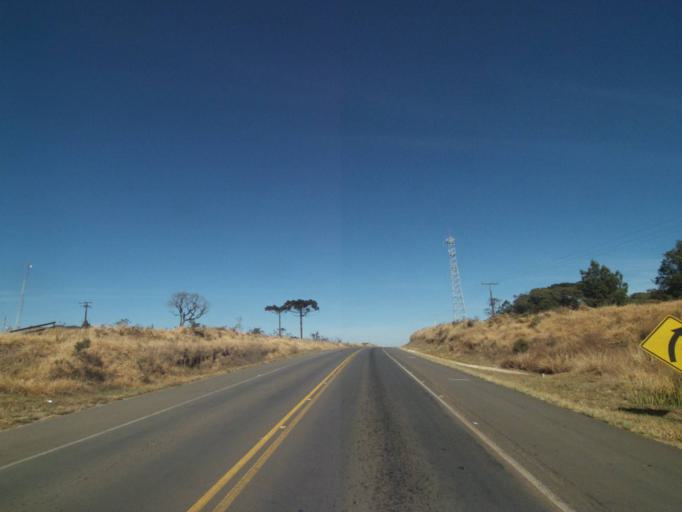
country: BR
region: Parana
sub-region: Tibagi
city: Tibagi
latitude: -24.7986
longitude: -50.4671
